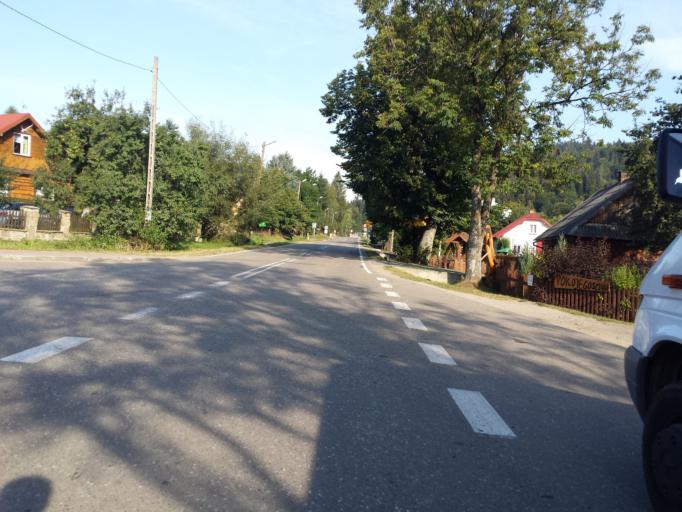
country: PL
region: Subcarpathian Voivodeship
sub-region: Powiat leski
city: Cisna
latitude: 49.2134
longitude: 22.3279
